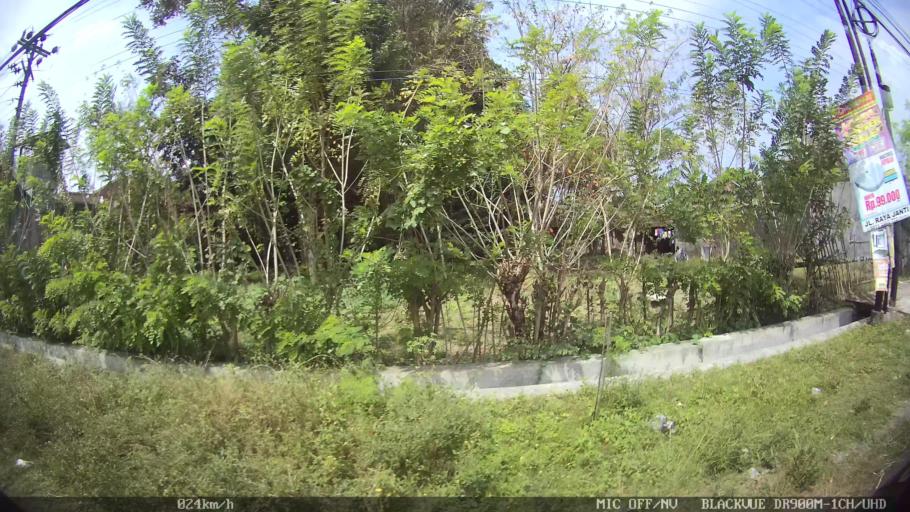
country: ID
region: Daerah Istimewa Yogyakarta
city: Depok
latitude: -7.7341
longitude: 110.4516
